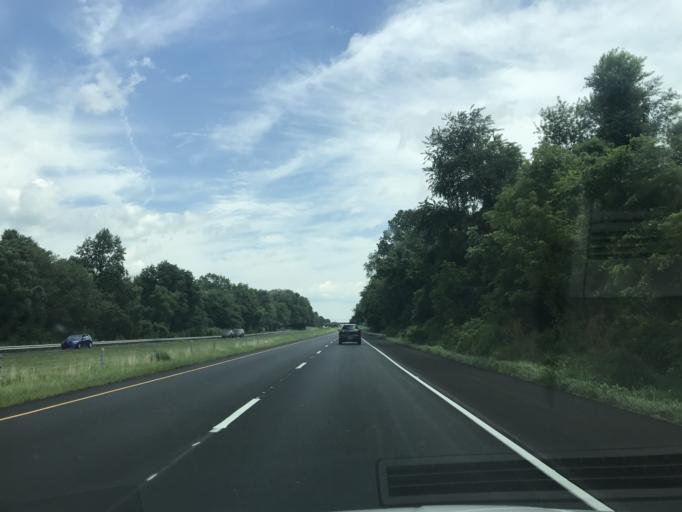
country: US
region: Pennsylvania
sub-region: Chester County
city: West Grove
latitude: 39.8263
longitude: -75.8789
